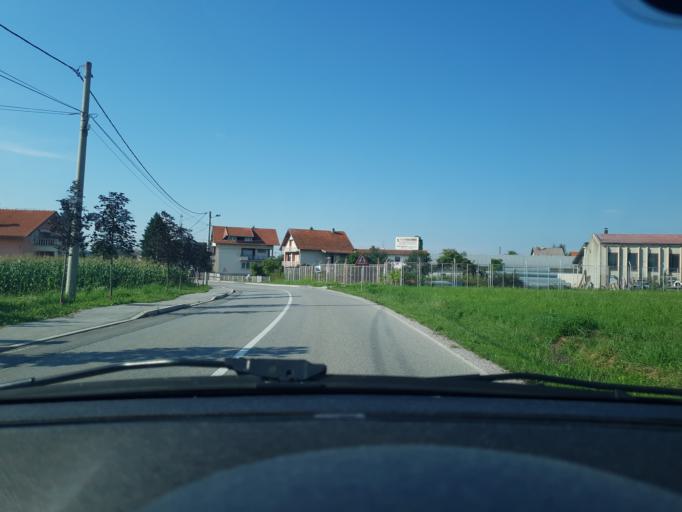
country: HR
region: Zagrebacka
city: Jablanovec
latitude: 45.8888
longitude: 15.8573
